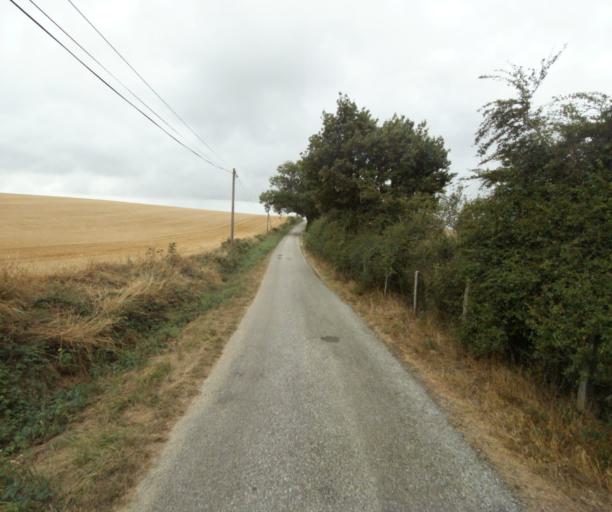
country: FR
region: Midi-Pyrenees
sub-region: Departement du Tarn
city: Soreze
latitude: 43.3947
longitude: 2.0520
